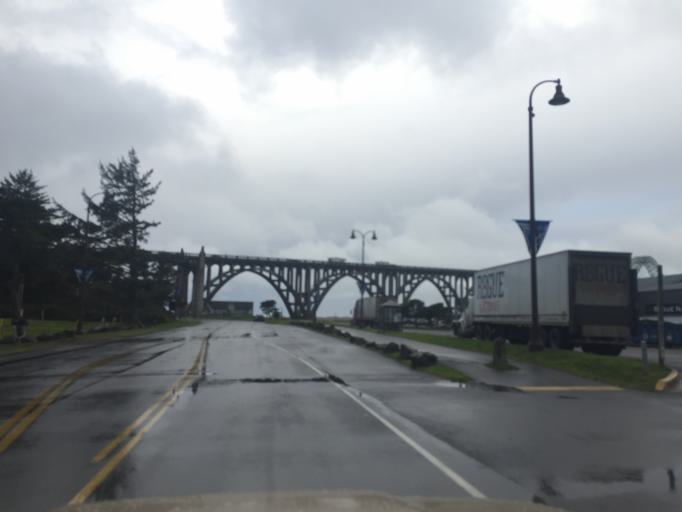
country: US
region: Oregon
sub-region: Lincoln County
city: Newport
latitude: 44.6194
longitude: -124.0506
